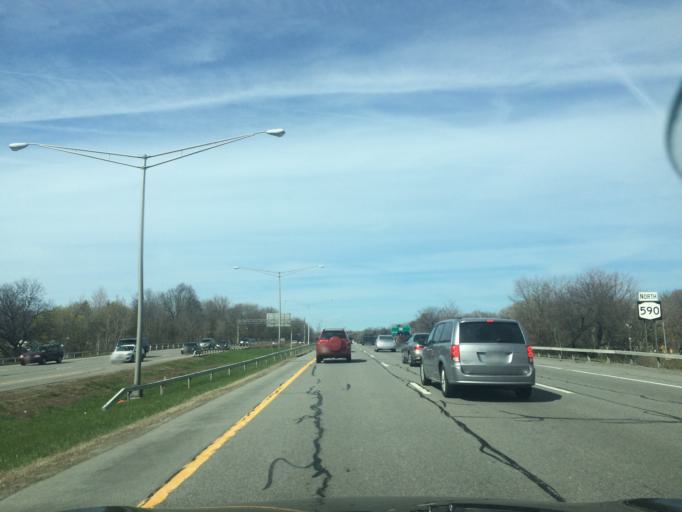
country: US
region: New York
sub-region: Monroe County
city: Brighton
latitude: 43.1480
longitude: -77.5405
